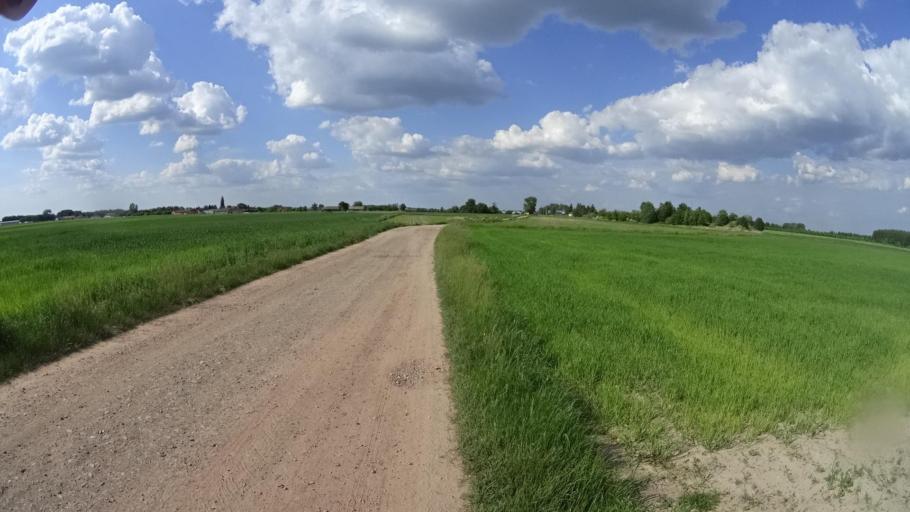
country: PL
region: Masovian Voivodeship
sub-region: Powiat piaseczynski
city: Tarczyn
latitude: 52.0250
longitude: 20.8176
